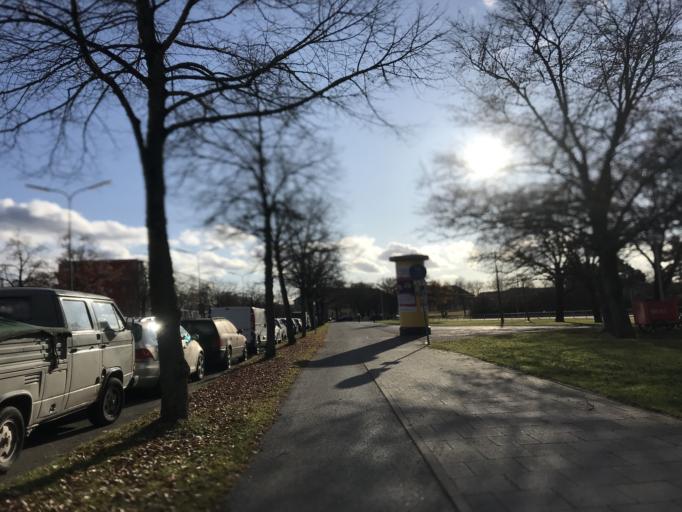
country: DE
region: Bavaria
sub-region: Upper Bavaria
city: Munich
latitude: 48.1637
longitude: 11.5528
